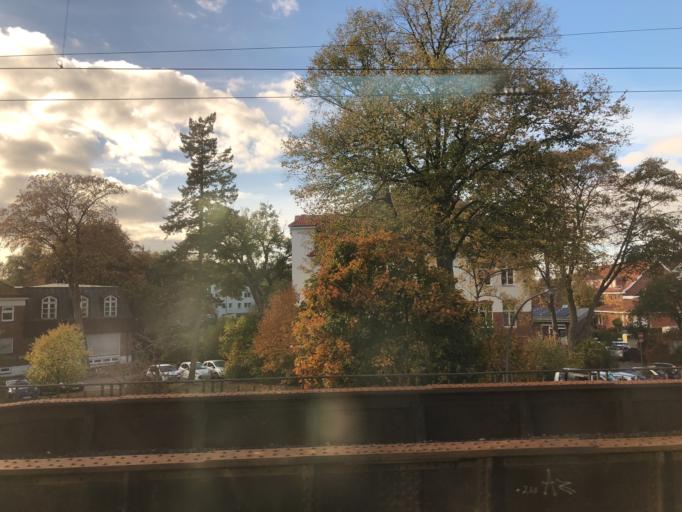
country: DE
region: Schleswig-Holstein
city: Neumunster
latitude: 54.0739
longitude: 9.9792
